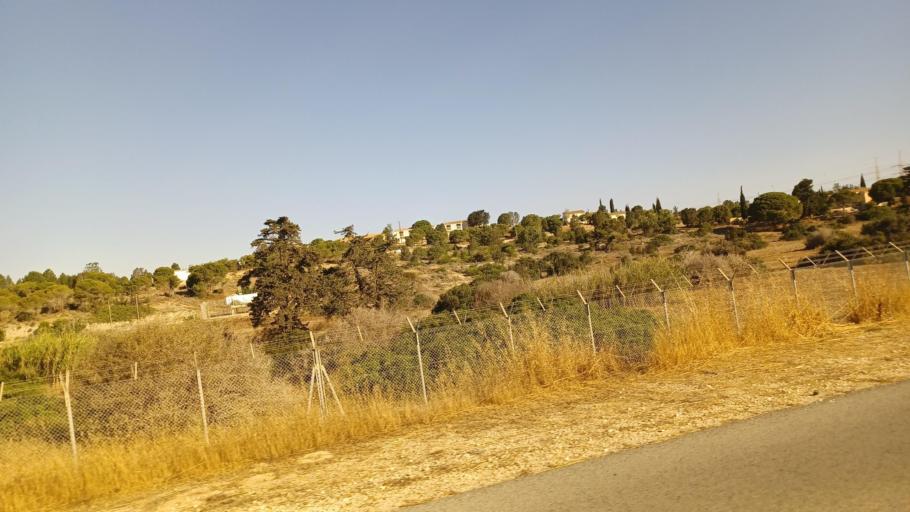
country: CY
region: Larnaka
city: Xylotymbou
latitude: 34.9855
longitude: 33.7417
